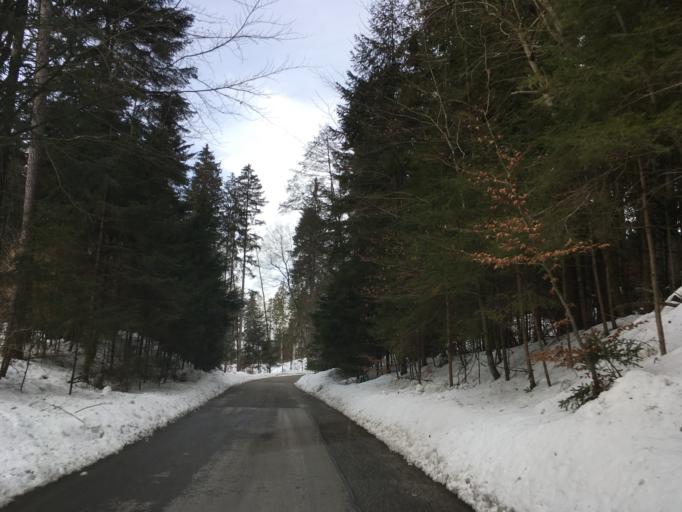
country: DE
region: Bavaria
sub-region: Upper Bavaria
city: Schnaitsee
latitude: 48.0426
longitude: 12.3616
